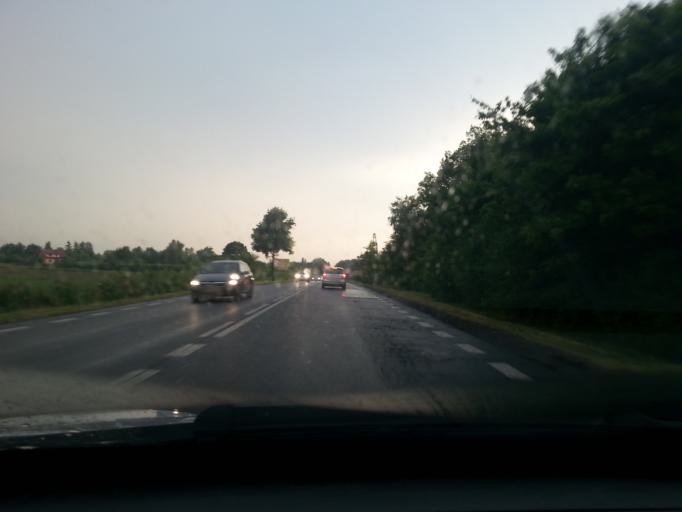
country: PL
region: Lodz Voivodeship
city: Lodz
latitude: 51.8281
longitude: 19.5270
